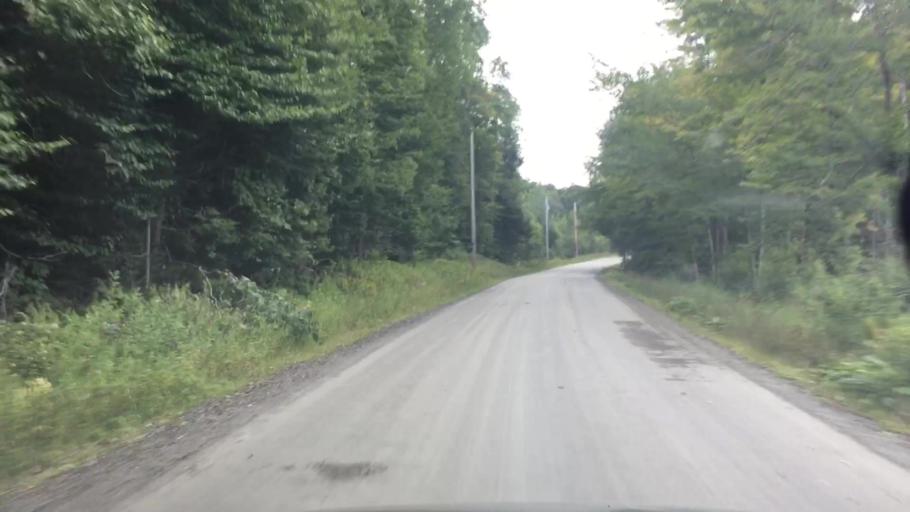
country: US
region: Vermont
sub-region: Windham County
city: Dover
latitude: 42.8376
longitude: -72.8127
